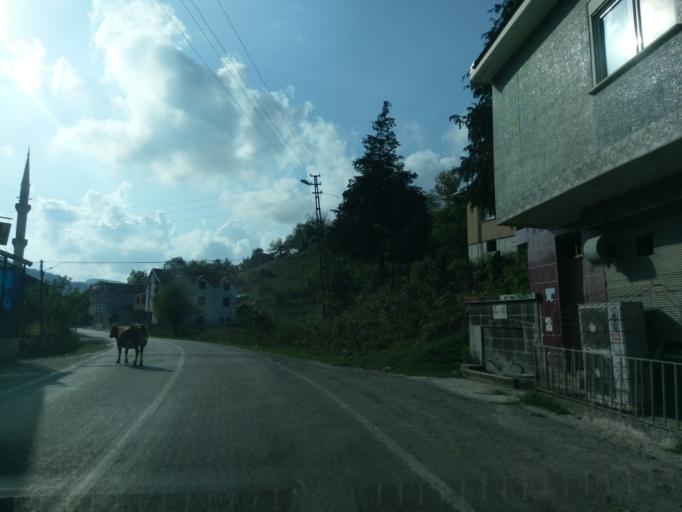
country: TR
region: Sinop
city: Helaldi
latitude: 41.9003
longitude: 34.4643
